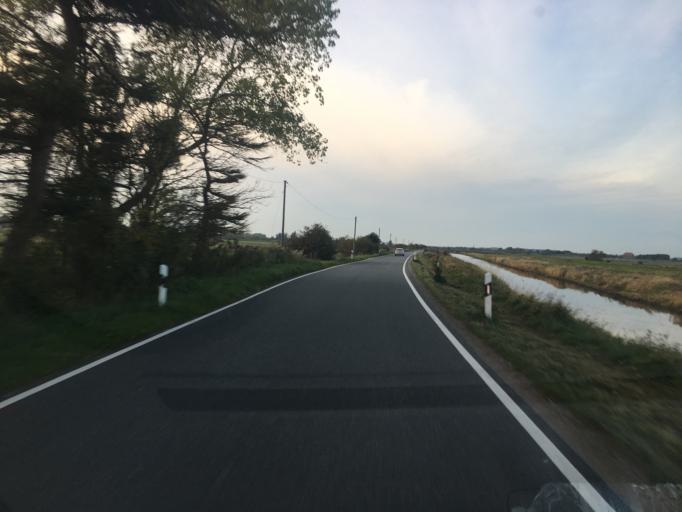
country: DE
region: Schleswig-Holstein
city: Aventoft
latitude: 54.9009
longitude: 8.8421
